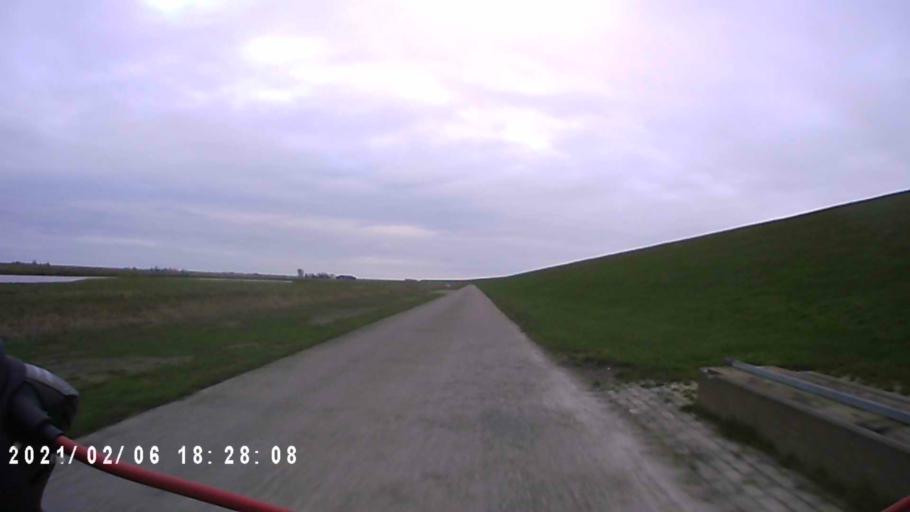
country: DE
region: Lower Saxony
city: Borkum
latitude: 53.4599
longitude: 6.6874
